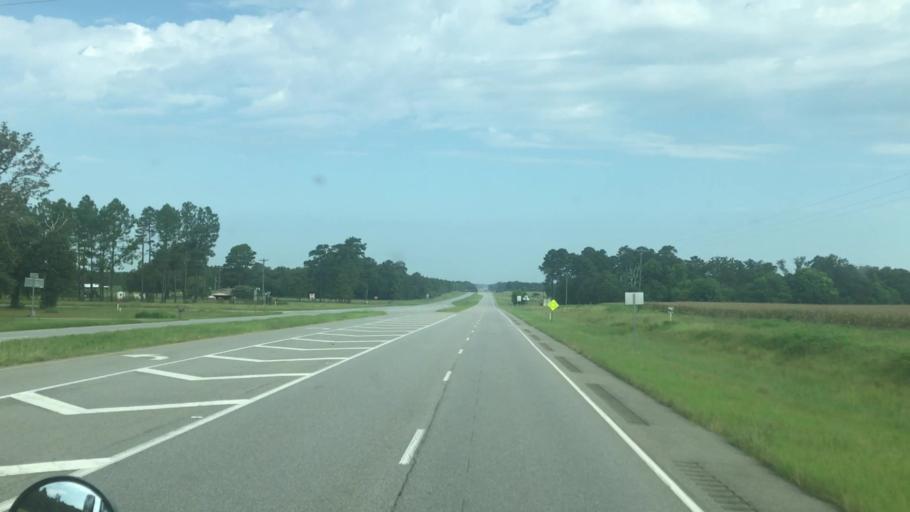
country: US
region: Georgia
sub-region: Early County
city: Blakely
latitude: 31.3204
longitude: -84.8821
